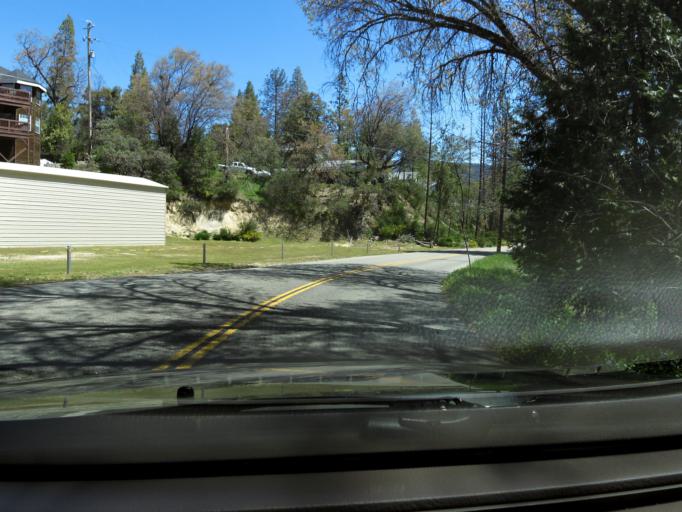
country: US
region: California
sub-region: Madera County
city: Oakhurst
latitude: 37.3208
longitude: -119.5607
